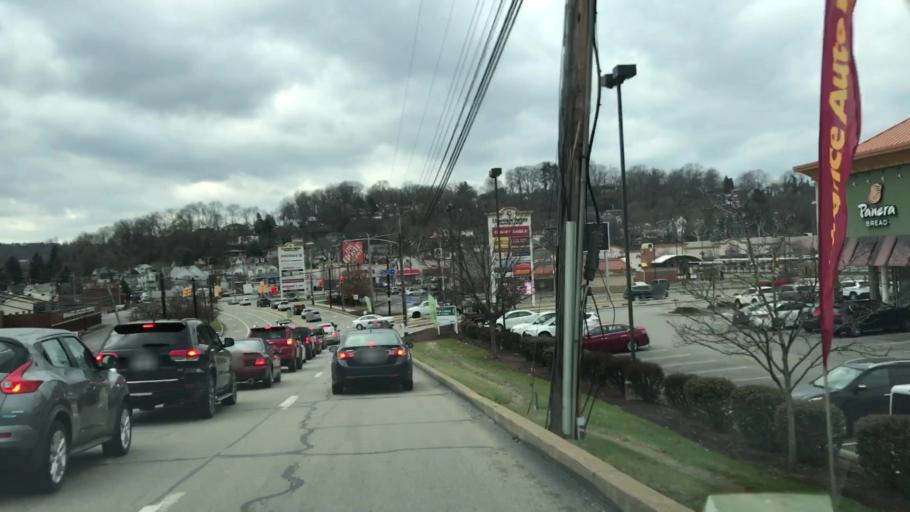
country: US
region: Pennsylvania
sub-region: Allegheny County
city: Bridgeville
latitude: 40.3659
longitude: -80.1075
